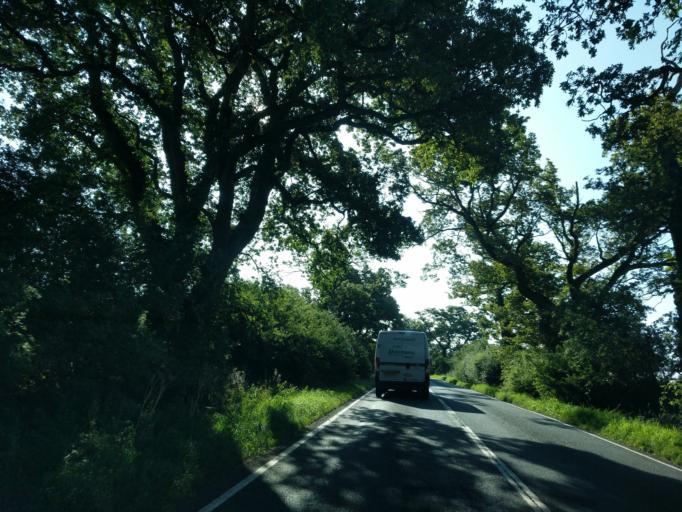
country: GB
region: England
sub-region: Lincolnshire
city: Bourne
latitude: 52.7992
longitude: -0.4695
